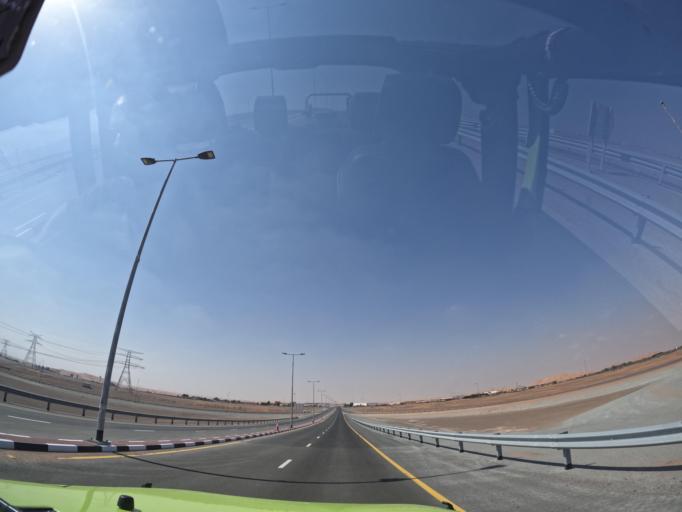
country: AE
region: Ash Shariqah
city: Adh Dhayd
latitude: 24.8136
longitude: 55.8014
